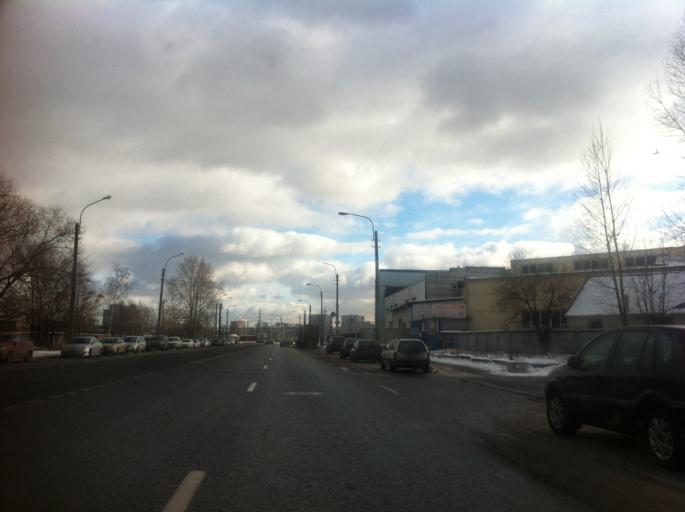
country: RU
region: St.-Petersburg
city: Avtovo
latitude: 59.8695
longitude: 30.2337
